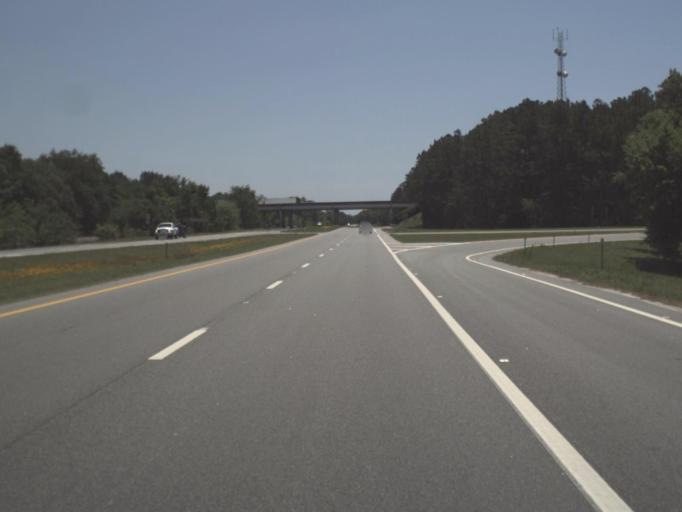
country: US
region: Florida
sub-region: Suwannee County
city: Live Oak
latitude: 30.3449
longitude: -83.0938
